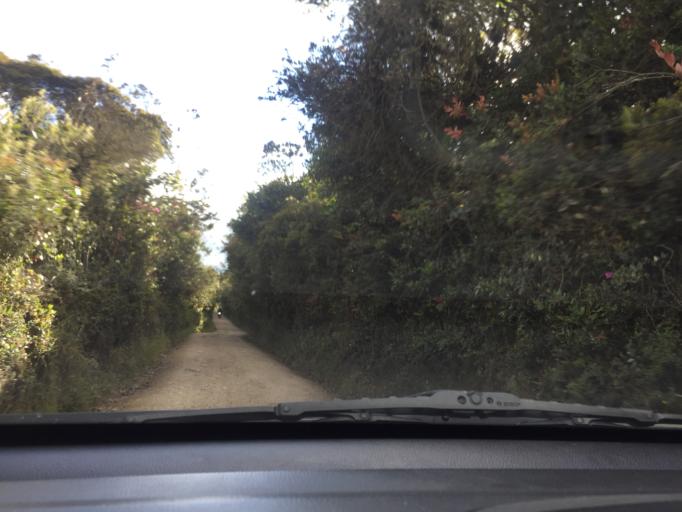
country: CO
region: Cundinamarca
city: Sopo
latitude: 4.9224
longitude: -73.9072
